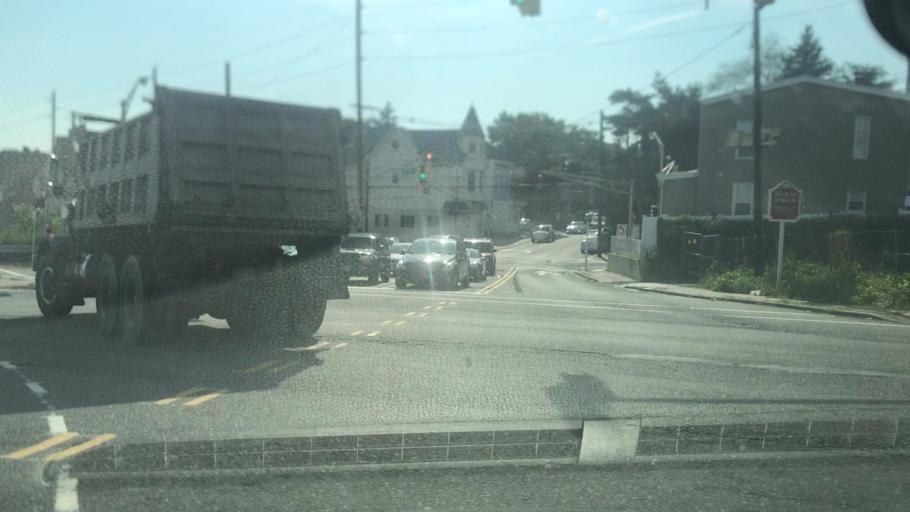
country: US
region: New Jersey
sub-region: Hudson County
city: Union City
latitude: 40.7790
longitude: -74.0379
